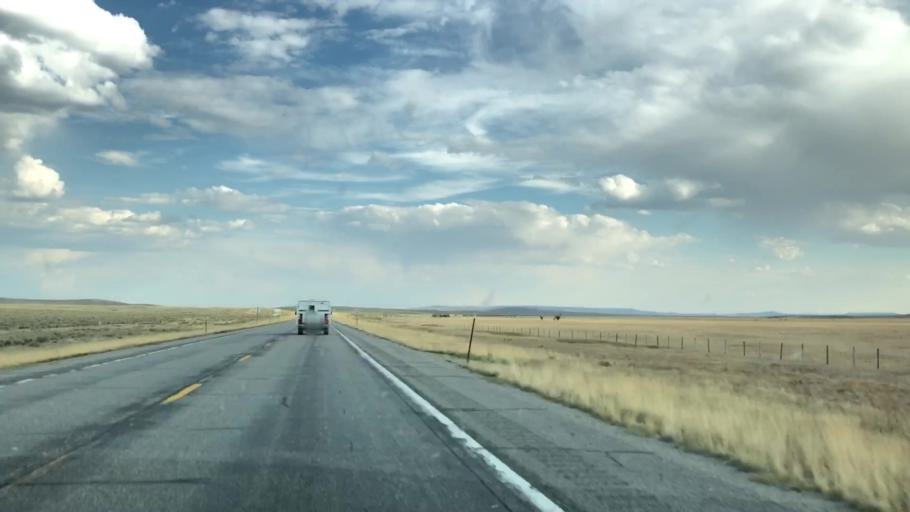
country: US
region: Wyoming
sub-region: Sublette County
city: Pinedale
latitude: 43.0420
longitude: -110.1414
